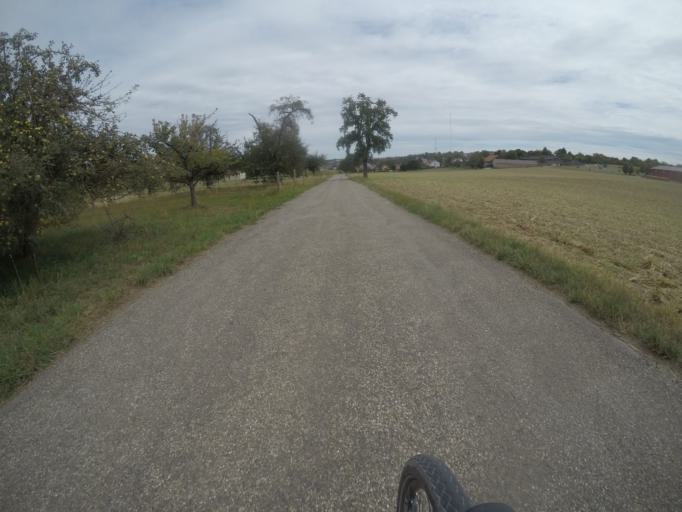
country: DE
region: Baden-Wuerttemberg
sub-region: Karlsruhe Region
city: Muhlacker
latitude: 48.9388
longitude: 8.8270
